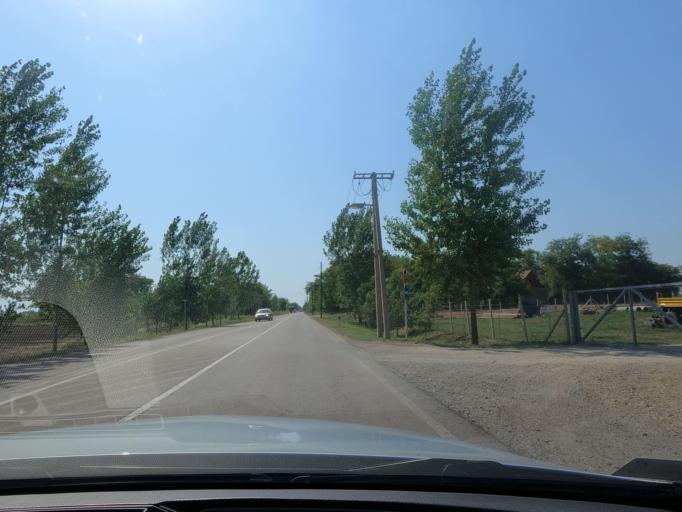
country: RS
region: Autonomna Pokrajina Vojvodina
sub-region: Severnobacki Okrug
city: Backa Topola
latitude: 45.8223
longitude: 19.6720
